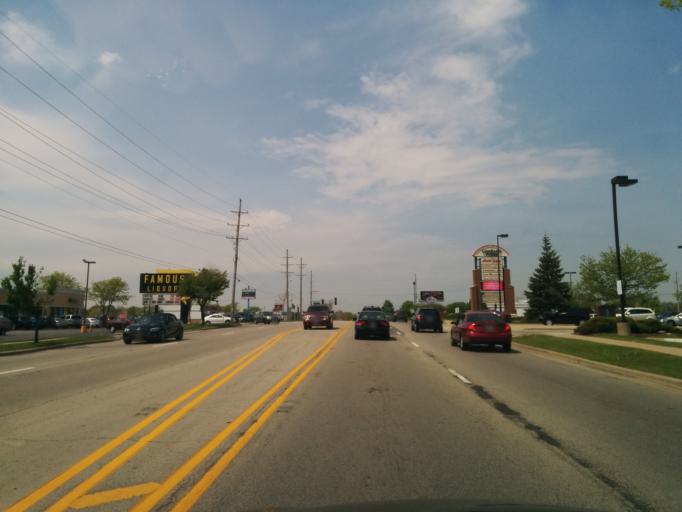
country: US
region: Illinois
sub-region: DuPage County
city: Lombard
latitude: 41.8602
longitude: -88.0150
